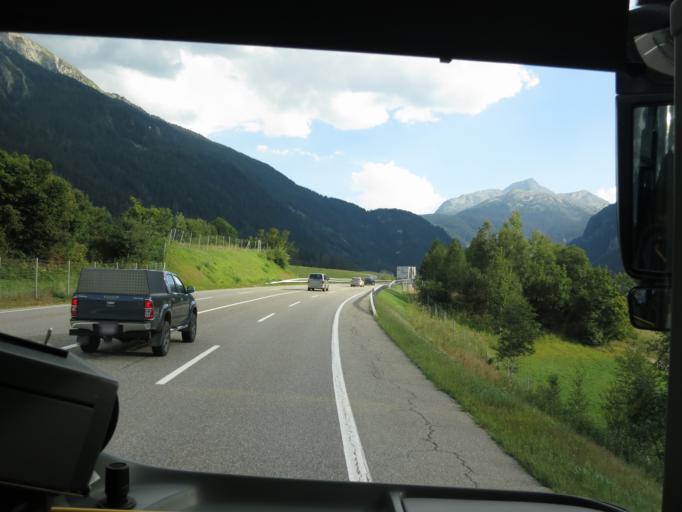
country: CH
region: Grisons
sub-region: Hinterrhein District
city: Thusis
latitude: 46.6173
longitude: 9.4332
